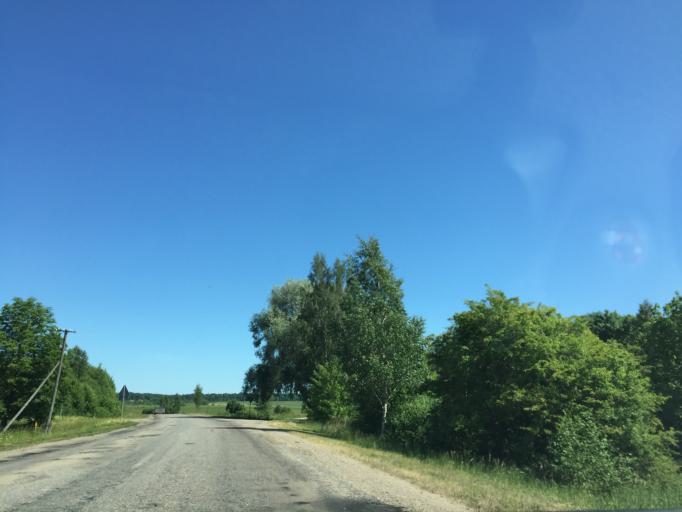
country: LV
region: Aizpute
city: Aizpute
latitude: 56.7336
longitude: 21.6955
